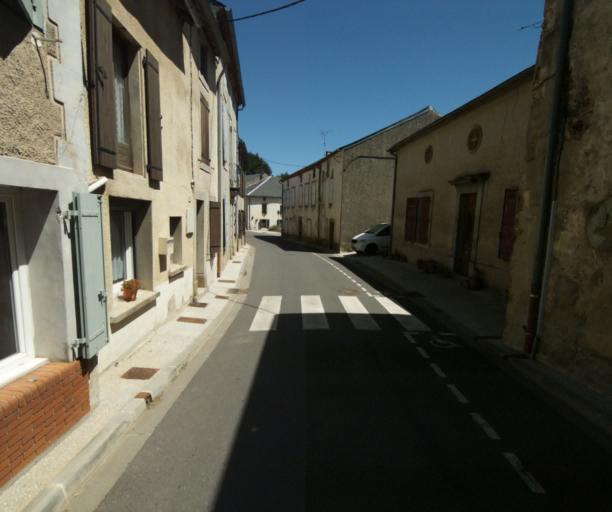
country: FR
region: Midi-Pyrenees
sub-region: Departement du Tarn
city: Dourgne
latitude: 43.4300
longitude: 2.1677
